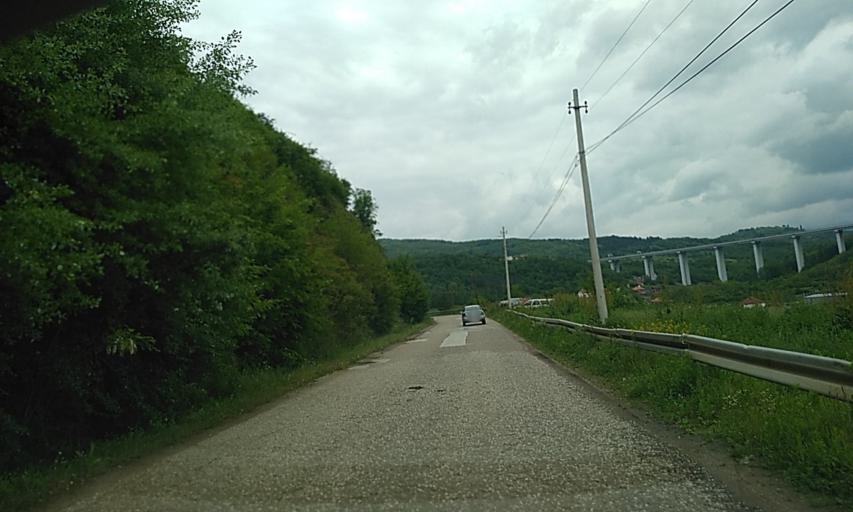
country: RS
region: Central Serbia
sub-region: Pcinjski Okrug
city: Vladicin Han
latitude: 42.7190
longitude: 22.0659
